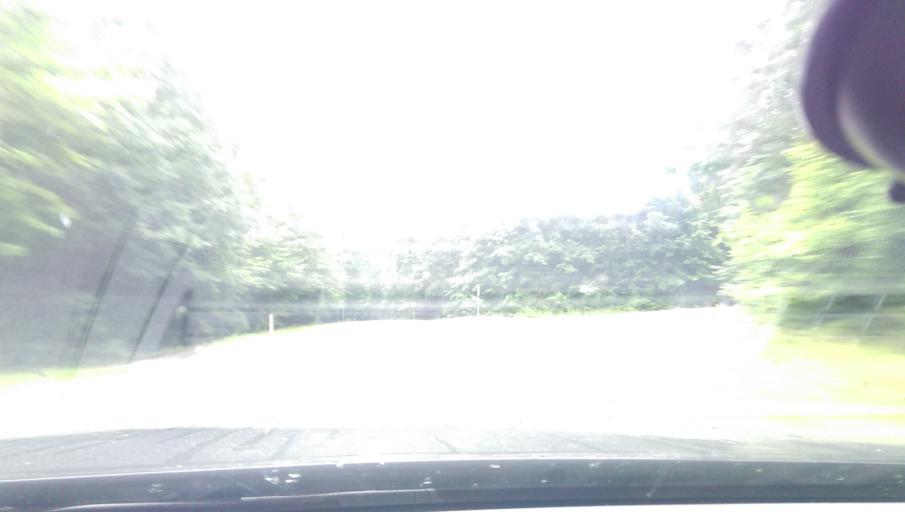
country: PL
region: Warmian-Masurian Voivodeship
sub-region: Powiat mragowski
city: Piecki
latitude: 53.7070
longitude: 21.4429
